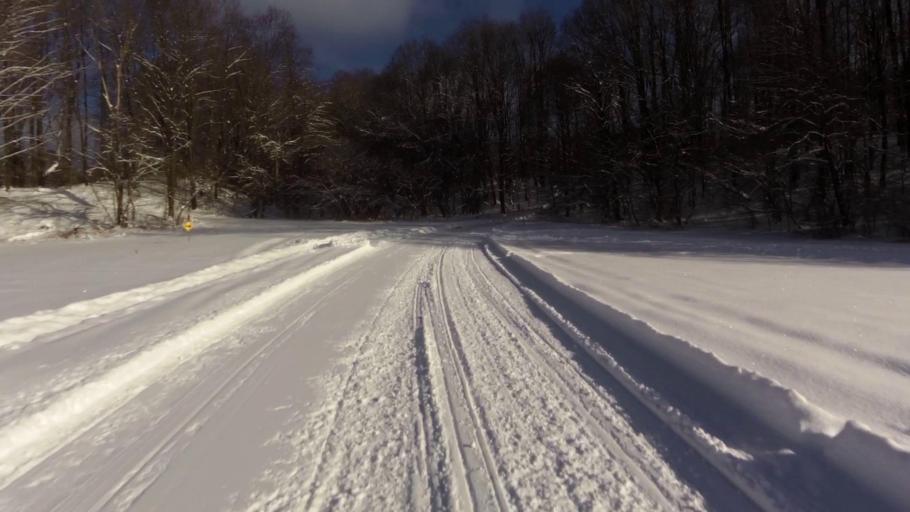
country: US
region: New York
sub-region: Chautauqua County
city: Falconer
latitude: 42.2535
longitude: -79.1438
